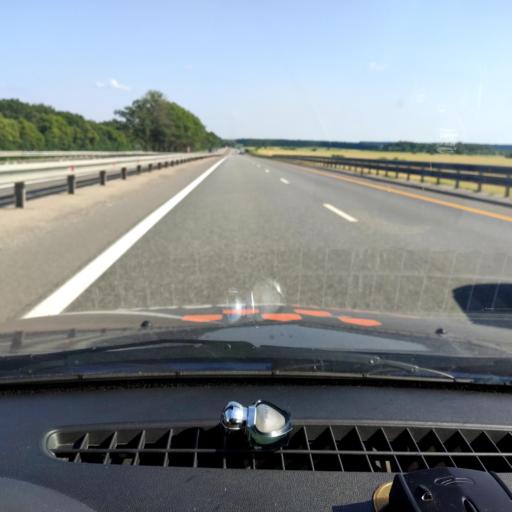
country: RU
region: Lipetsk
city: Zadonsk
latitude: 52.4578
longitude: 38.7759
